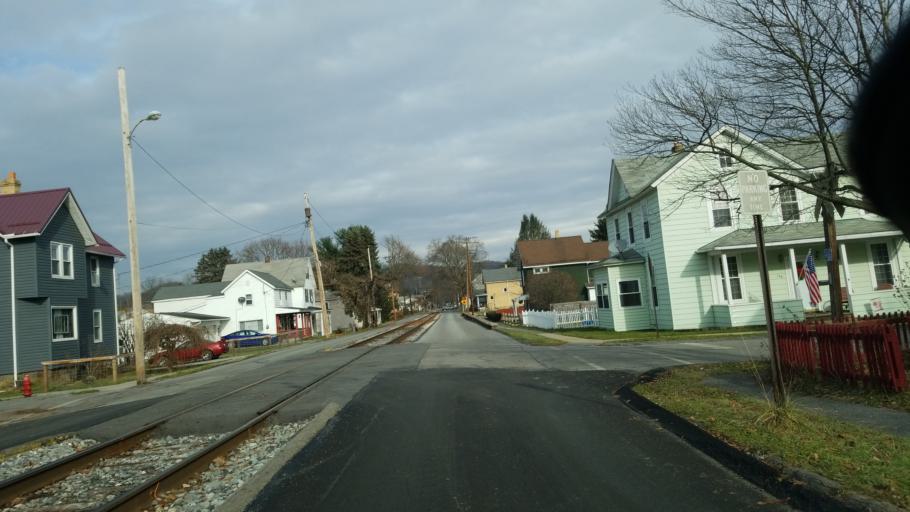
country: US
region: Pennsylvania
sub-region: Clearfield County
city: Clearfield
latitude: 41.0256
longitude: -78.4417
